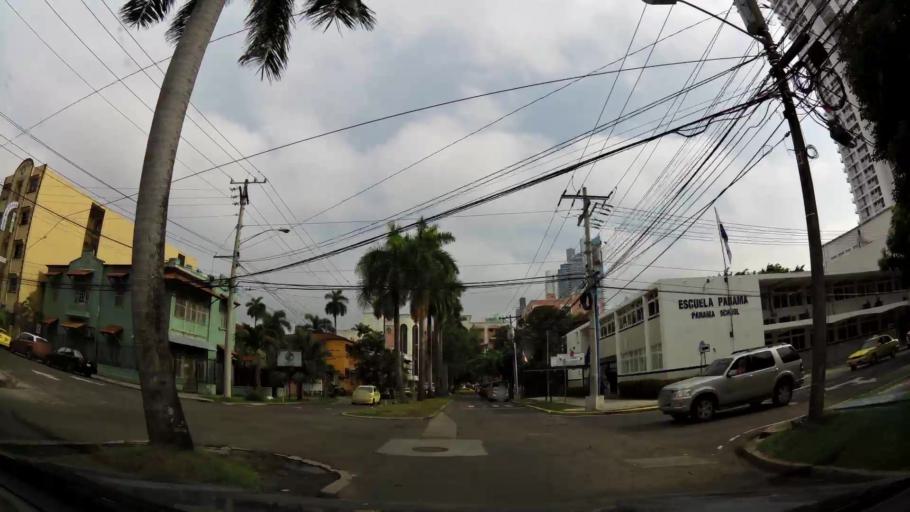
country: PA
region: Panama
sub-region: Distrito de Panama
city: Ancon
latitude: 8.9678
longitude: -79.5343
